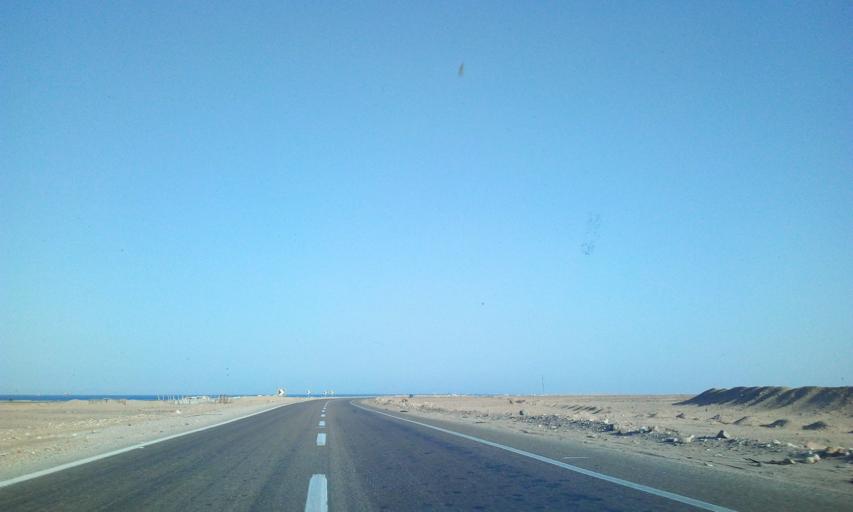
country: EG
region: South Sinai
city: Tor
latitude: 28.5377
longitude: 32.9220
